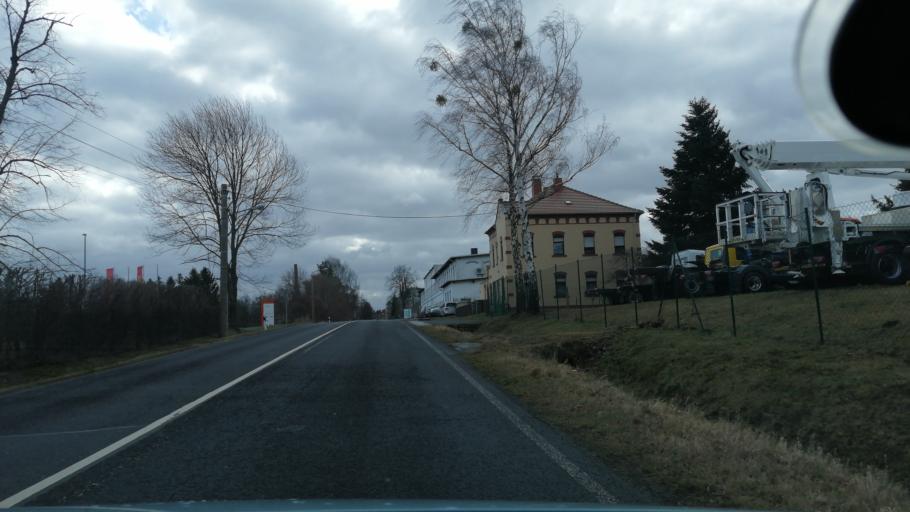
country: DE
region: Saxony
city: Lobau
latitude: 51.1022
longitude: 14.6562
